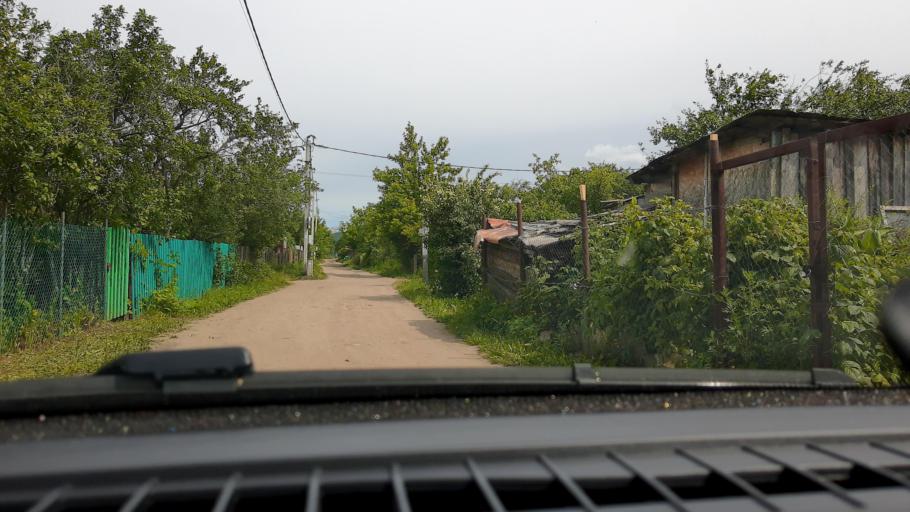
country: RU
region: Nizjnij Novgorod
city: Nizhniy Novgorod
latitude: 56.2678
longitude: 43.9543
